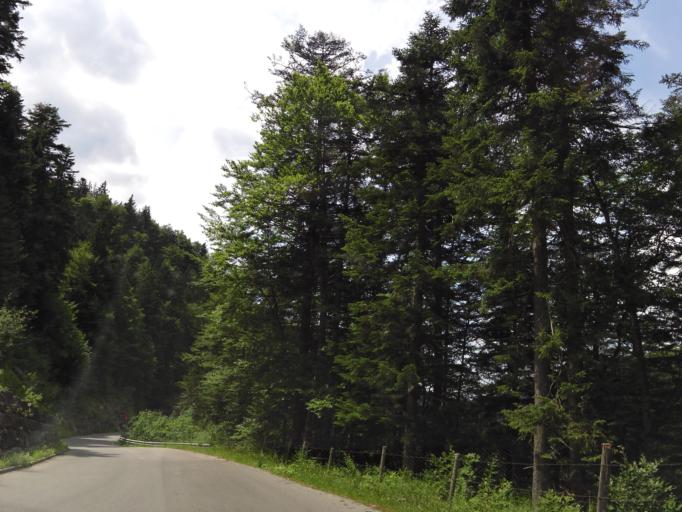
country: AT
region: Tyrol
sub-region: Politischer Bezirk Kitzbuhel
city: Waidring
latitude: 47.6629
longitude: 12.5669
